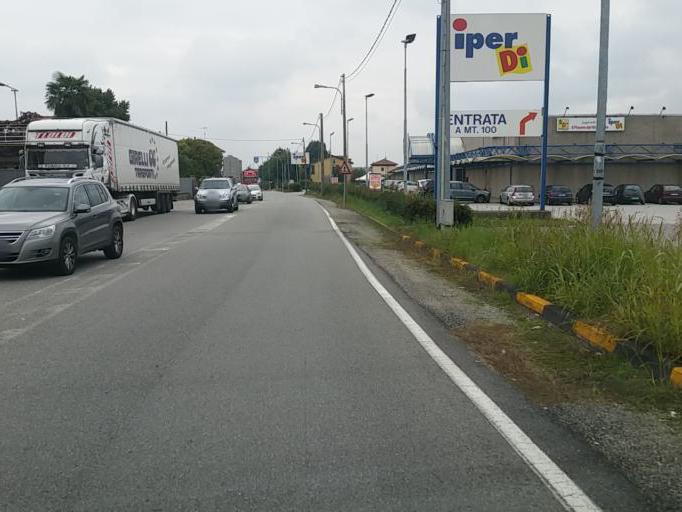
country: IT
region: Piedmont
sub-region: Provincia di Novara
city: Gozzano
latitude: 45.7353
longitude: 8.4404
